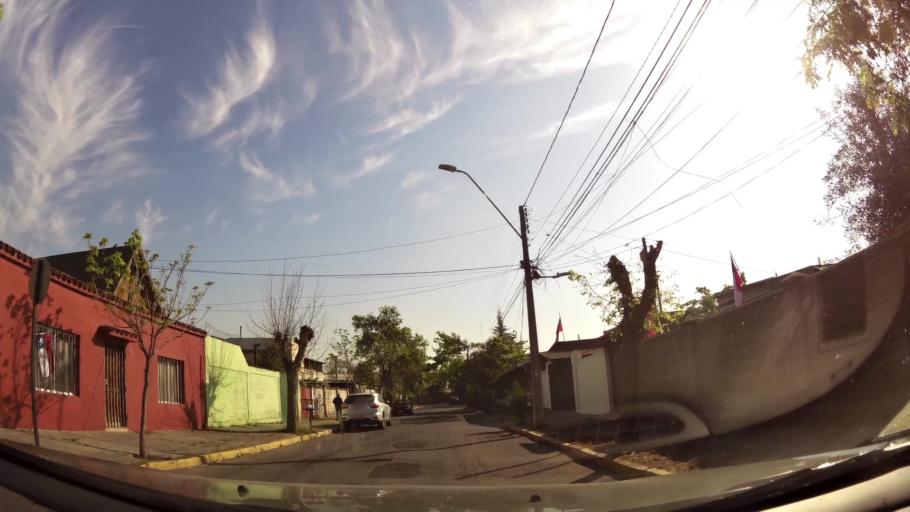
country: CL
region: Santiago Metropolitan
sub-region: Provincia de Maipo
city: San Bernardo
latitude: -33.5969
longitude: -70.7140
